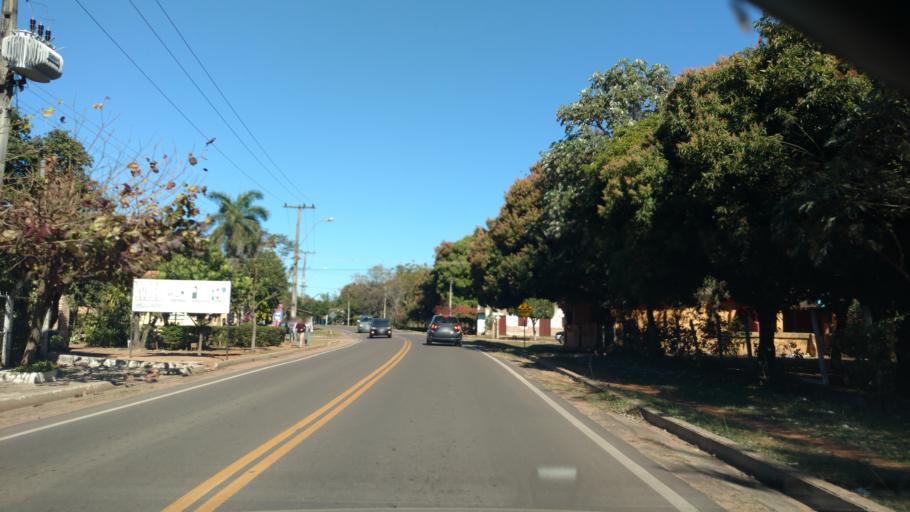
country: PY
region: Paraguari
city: Pirayu
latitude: -25.4883
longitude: -57.2381
